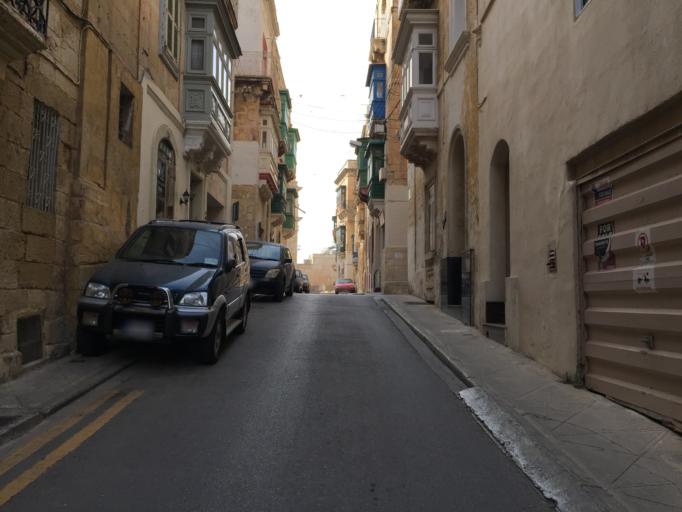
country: MT
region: L-Isla
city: Senglea
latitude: 35.8892
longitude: 14.5160
